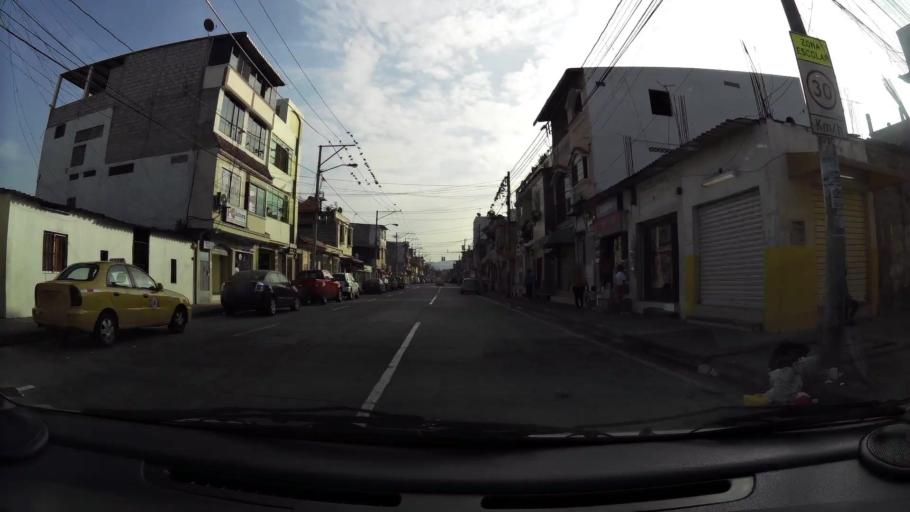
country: EC
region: Guayas
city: Eloy Alfaro
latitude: -2.1256
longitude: -79.8961
